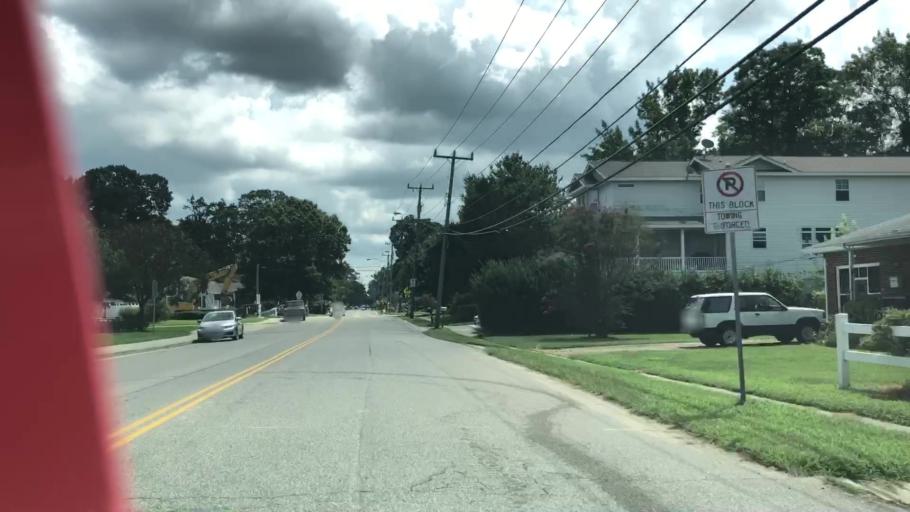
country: US
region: Virginia
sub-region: City of Virginia Beach
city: Virginia Beach
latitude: 36.8422
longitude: -75.9806
